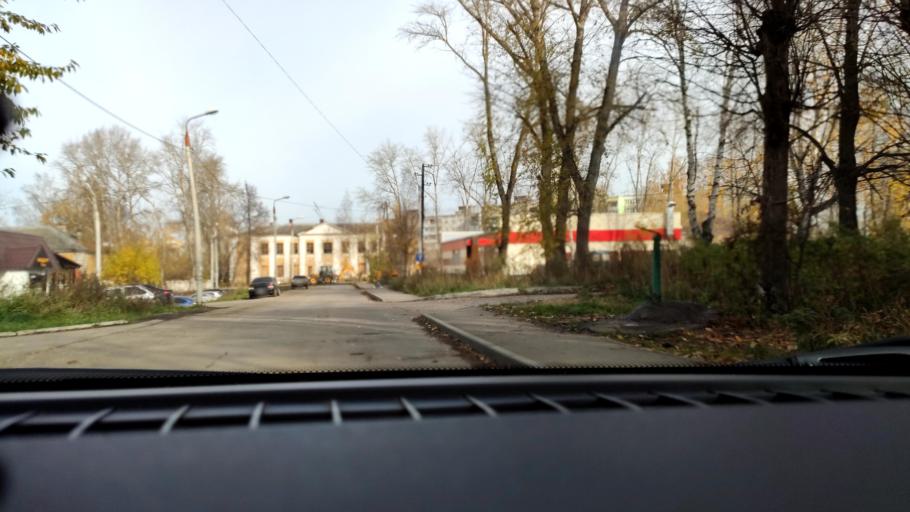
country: RU
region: Perm
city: Perm
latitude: 58.1110
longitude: 56.3760
